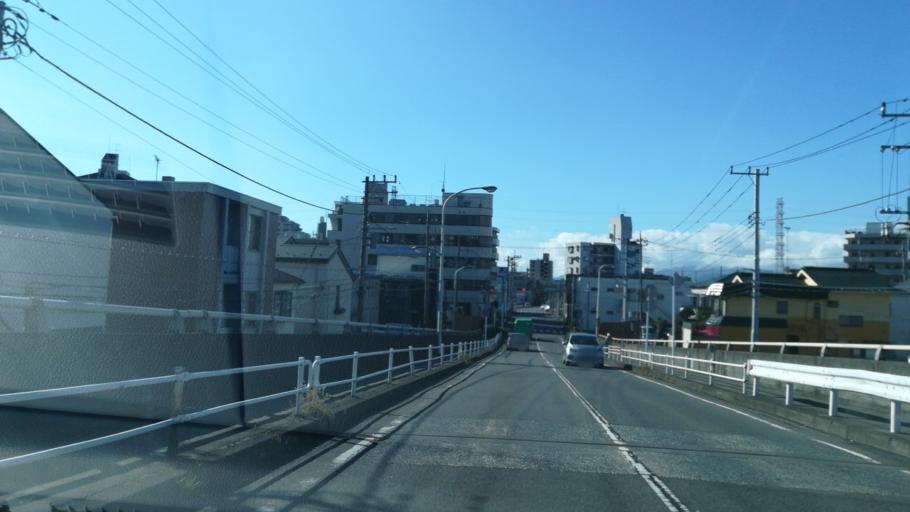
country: JP
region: Tokyo
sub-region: Machida-shi
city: Machida
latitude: 35.5706
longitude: 139.3904
